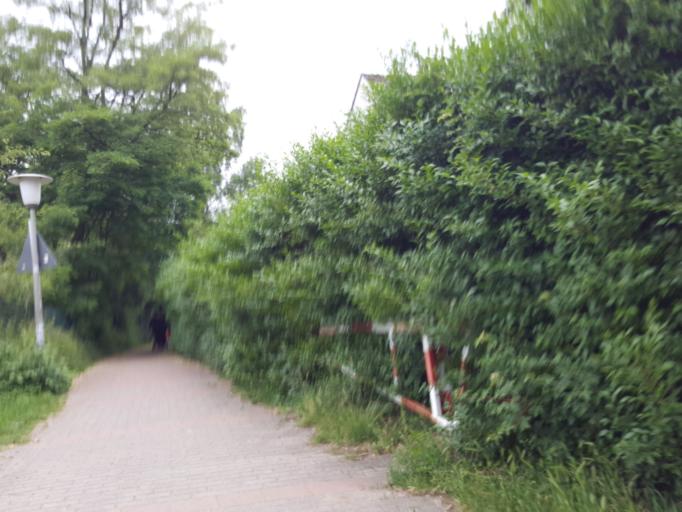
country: DE
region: Hamburg
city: Wandsbek
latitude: 53.5406
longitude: 10.1138
